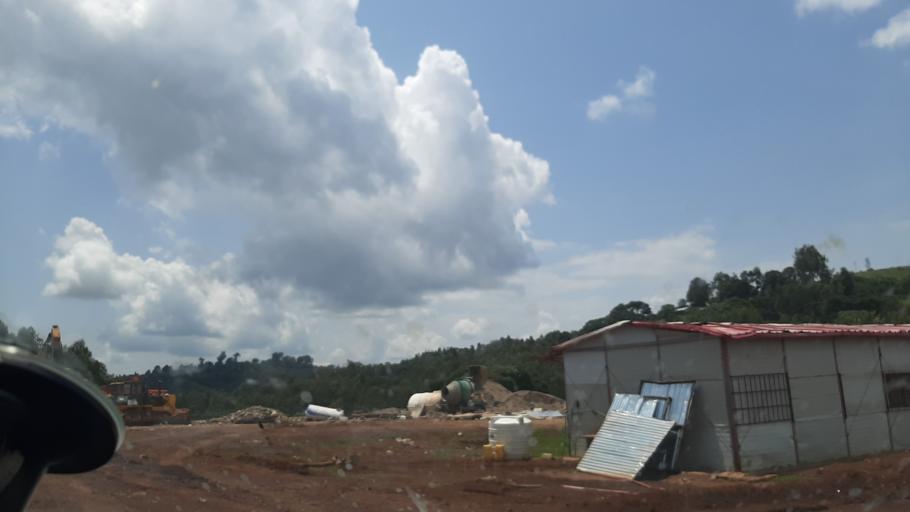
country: ET
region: Oromiya
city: Agaro
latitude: 7.9403
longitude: 36.8407
